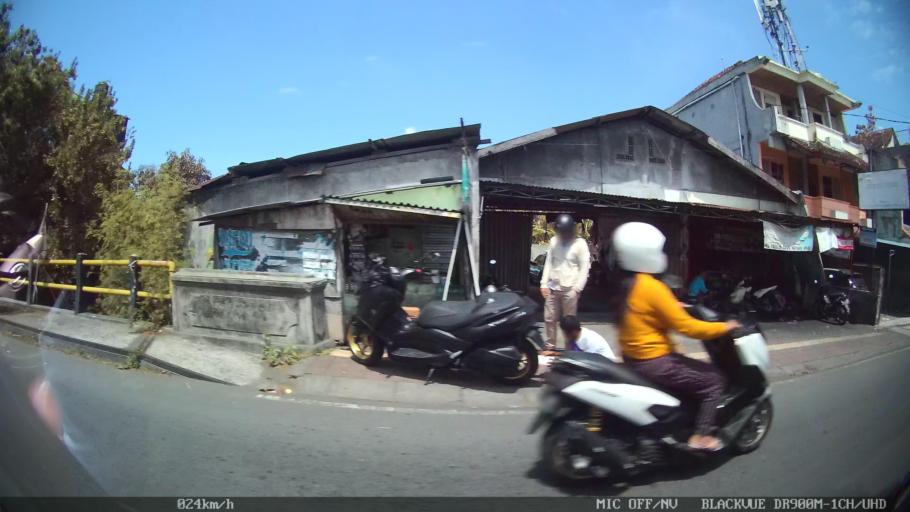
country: ID
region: Bali
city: Denpasar
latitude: -8.6679
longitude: 115.1999
